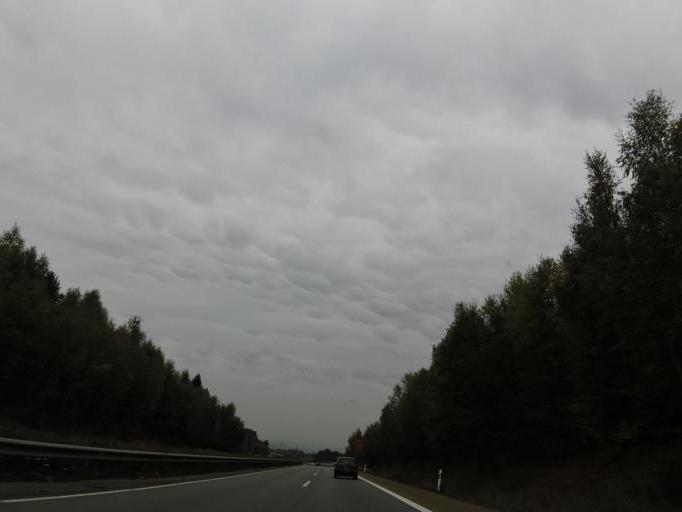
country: DE
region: Rheinland-Pfalz
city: Sembach
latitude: 49.5132
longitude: 7.8460
